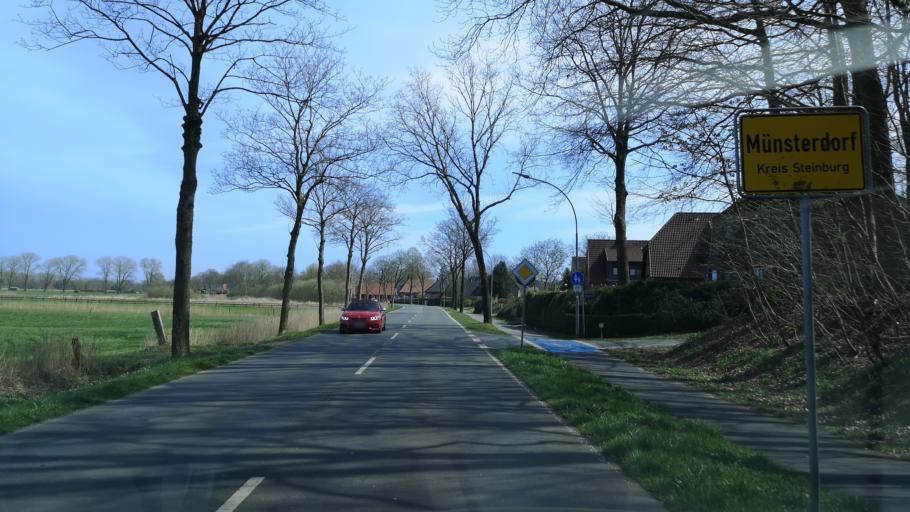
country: DE
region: Schleswig-Holstein
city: Munsterdorf
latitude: 53.9053
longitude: 9.5281
